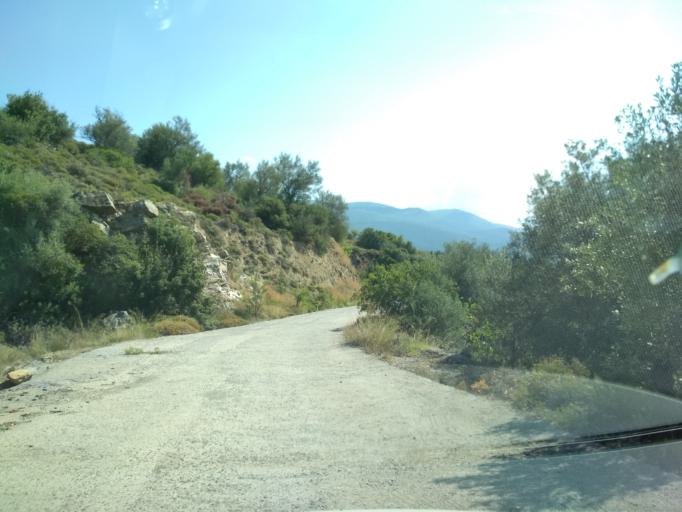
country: GR
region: Central Greece
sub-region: Nomos Evvoias
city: Oreoi
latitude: 38.8523
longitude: 23.1081
